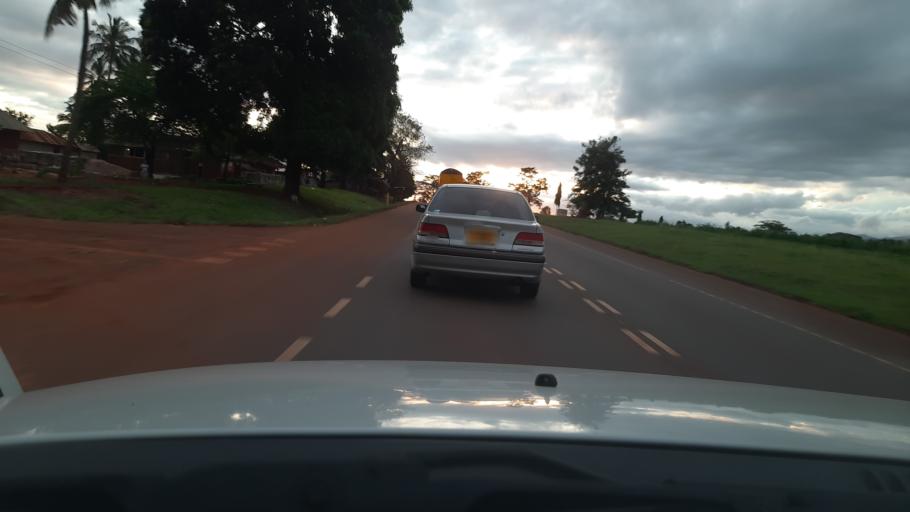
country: TZ
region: Tanga
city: Muheza
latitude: -5.1411
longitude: 38.8658
